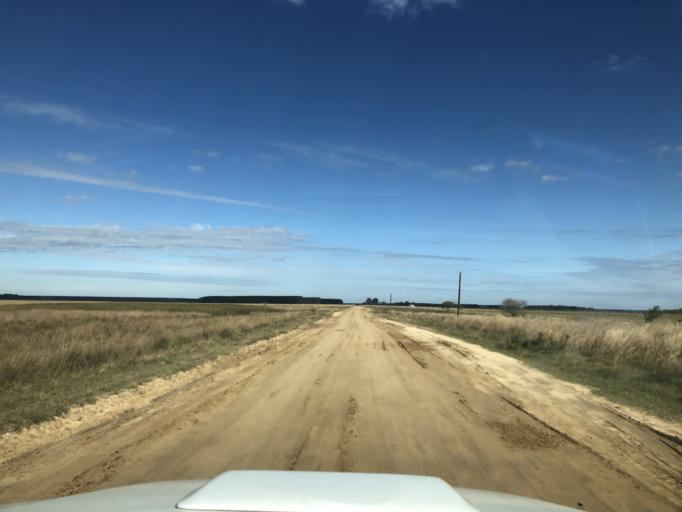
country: AR
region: Corrientes
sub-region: Departamento de Concepcion
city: Concepcion
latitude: -28.4964
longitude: -58.0380
